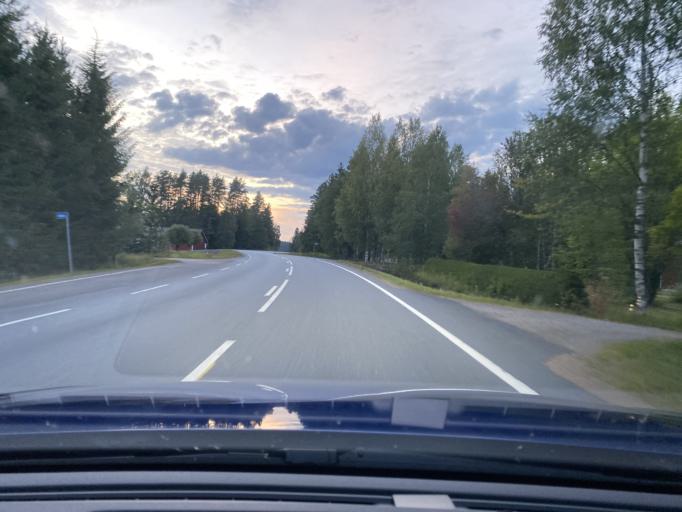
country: FI
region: Satakunta
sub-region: Pohjois-Satakunta
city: Honkajoki
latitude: 62.2184
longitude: 22.2869
